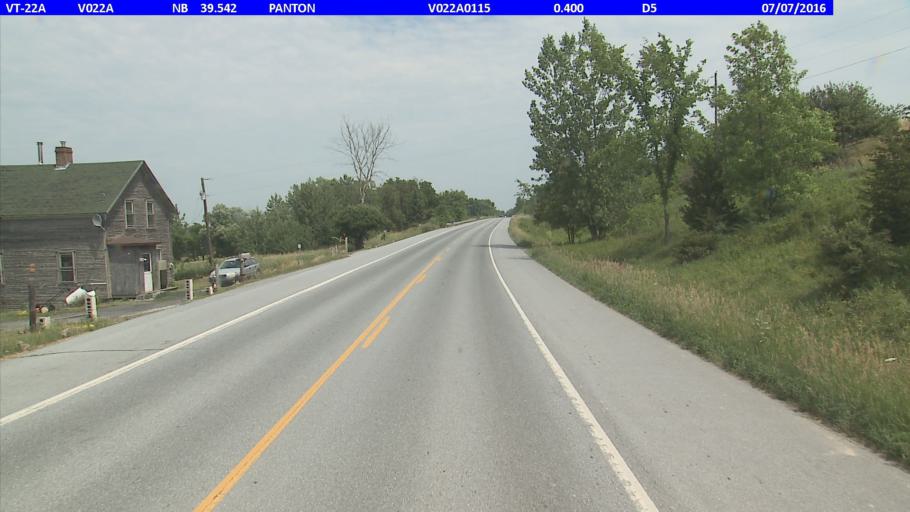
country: US
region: Vermont
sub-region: Addison County
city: Vergennes
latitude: 44.1252
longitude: -73.2918
